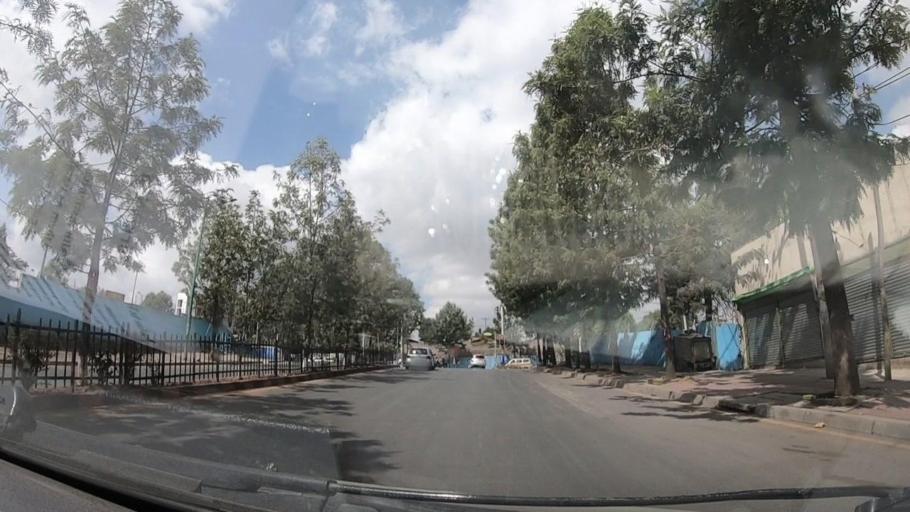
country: ET
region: Adis Abeba
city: Addis Ababa
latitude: 9.0035
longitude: 38.7342
